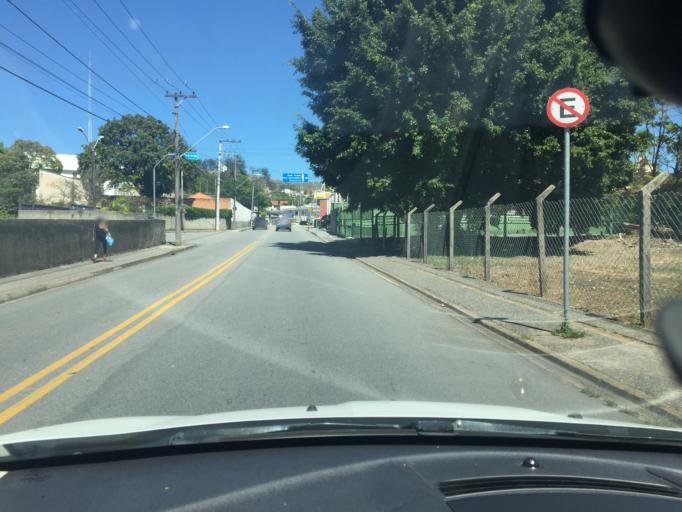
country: BR
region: Sao Paulo
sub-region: Jundiai
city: Jundiai
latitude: -23.2058
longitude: -46.8836
